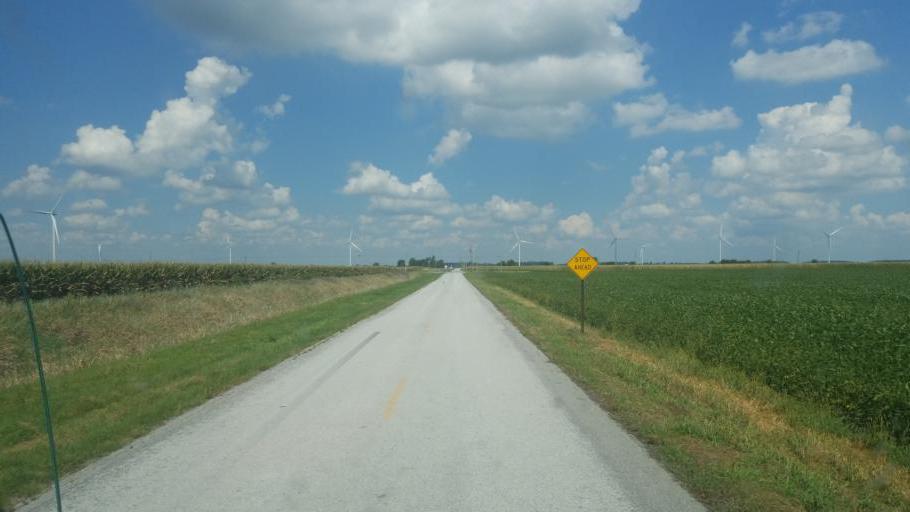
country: US
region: Ohio
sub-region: Hardin County
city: Ada
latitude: 40.7739
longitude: -83.7286
